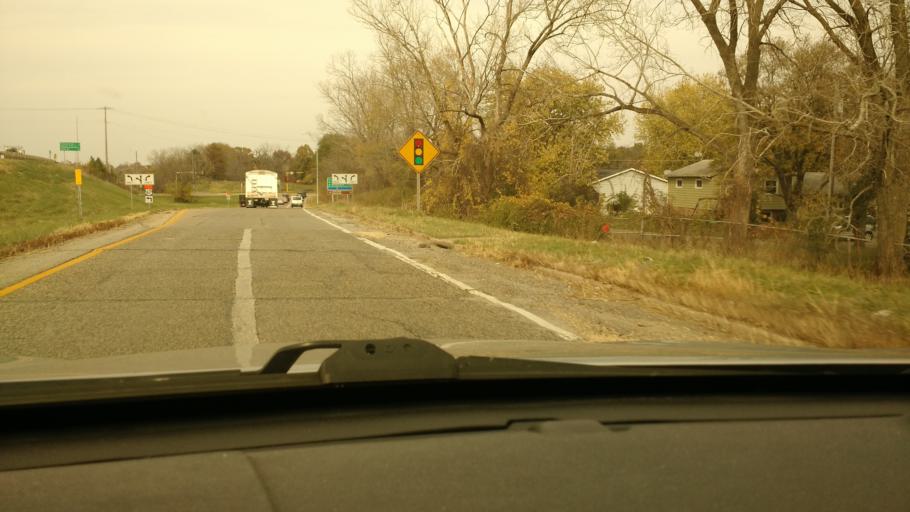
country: US
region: Iowa
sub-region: Scott County
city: Bettendorf
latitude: 41.5392
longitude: -90.5170
